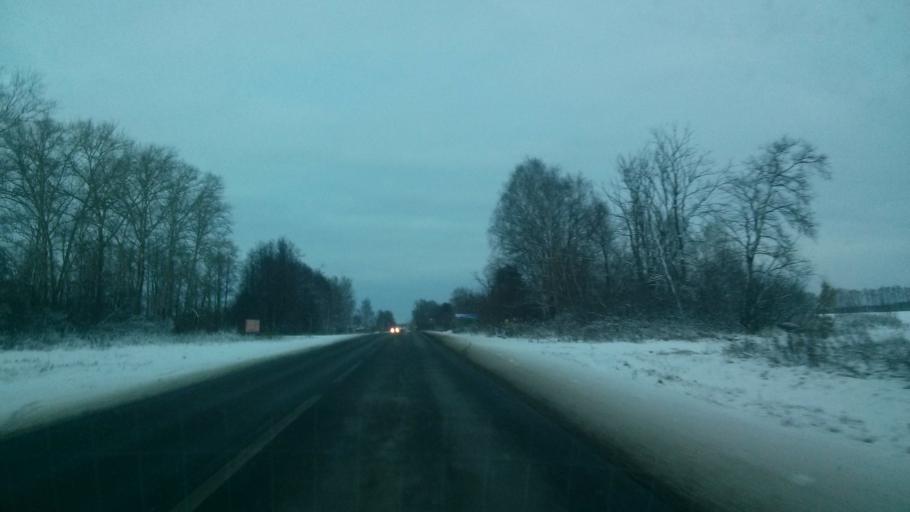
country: RU
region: Nizjnij Novgorod
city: Bogorodsk
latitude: 56.0573
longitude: 43.4135
